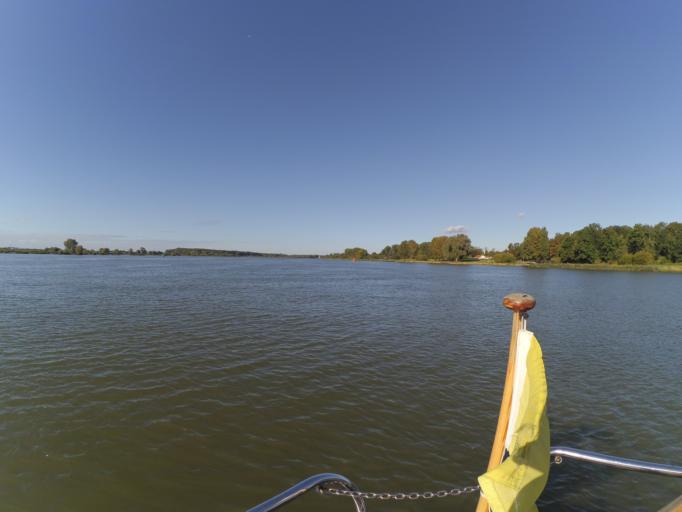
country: NL
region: South Holland
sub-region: Gemeente Zwijndrecht
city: Heerjansdam
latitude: 51.8326
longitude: 4.5427
